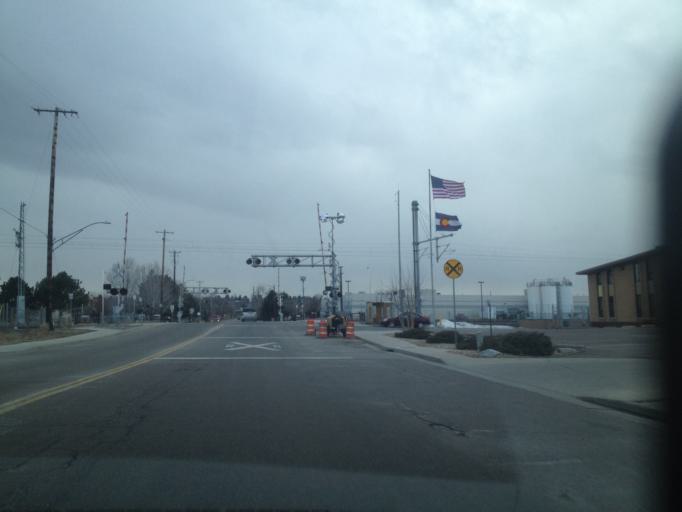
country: US
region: Colorado
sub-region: Adams County
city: Berkley
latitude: 39.8053
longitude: -105.0441
